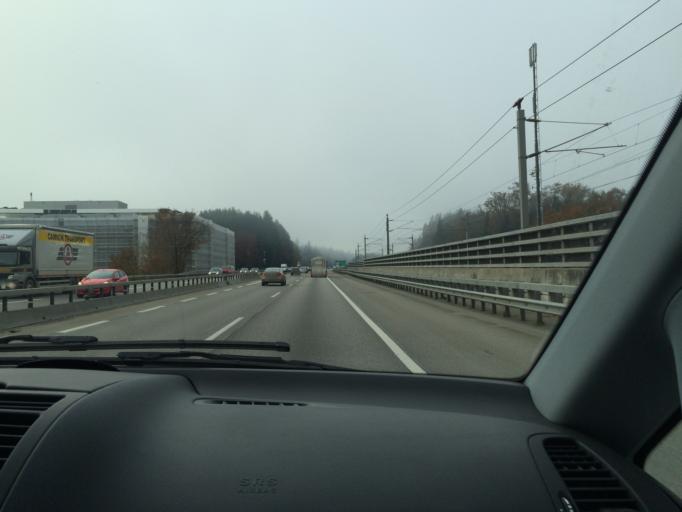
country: CH
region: Bern
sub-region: Emmental District
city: Lyssach
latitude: 47.0710
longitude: 7.5660
